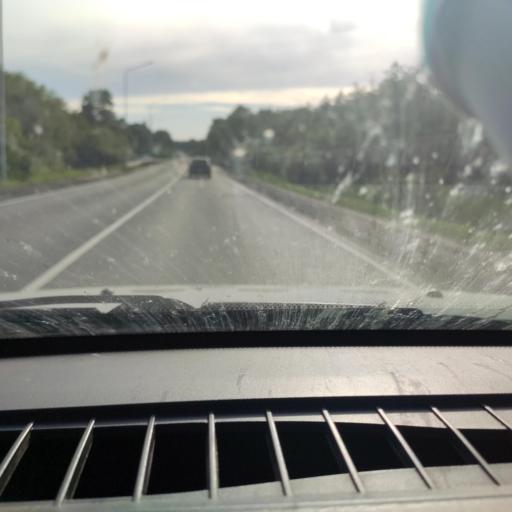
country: RU
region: Kirov
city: Vakhrushi
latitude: 58.6514
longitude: 49.8811
